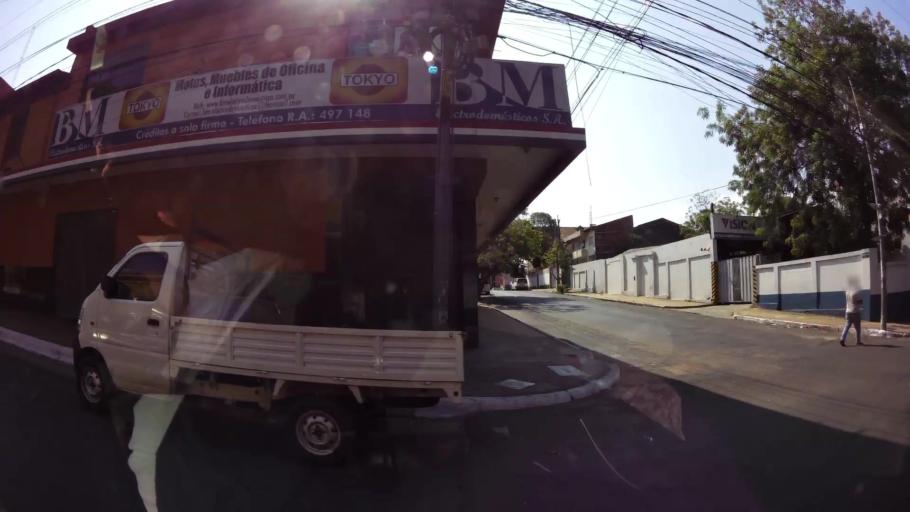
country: PY
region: Asuncion
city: Asuncion
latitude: -25.2907
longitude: -57.6287
